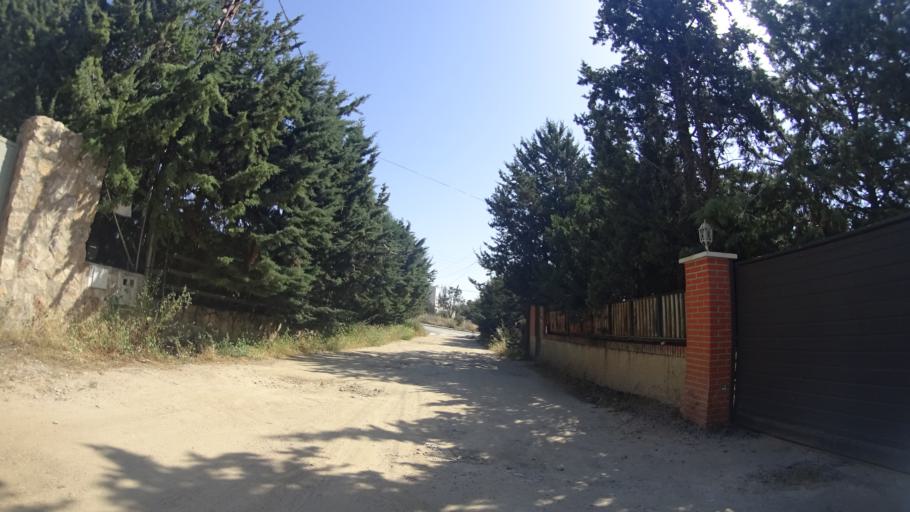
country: ES
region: Madrid
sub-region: Provincia de Madrid
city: Hoyo de Manzanares
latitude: 40.6014
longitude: -3.9107
